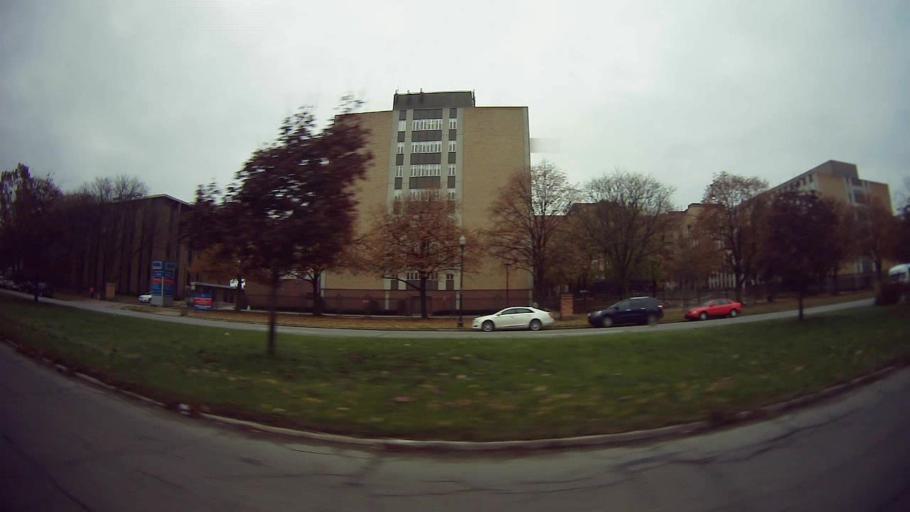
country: US
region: Michigan
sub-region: Oakland County
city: Oak Park
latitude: 42.4203
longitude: -83.1820
